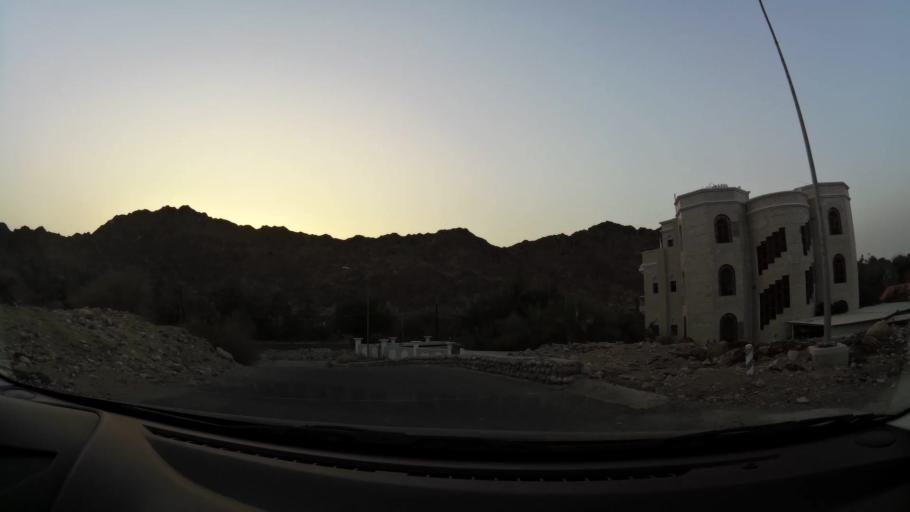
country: OM
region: Muhafazat Masqat
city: Bawshar
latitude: 23.4771
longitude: 58.3266
